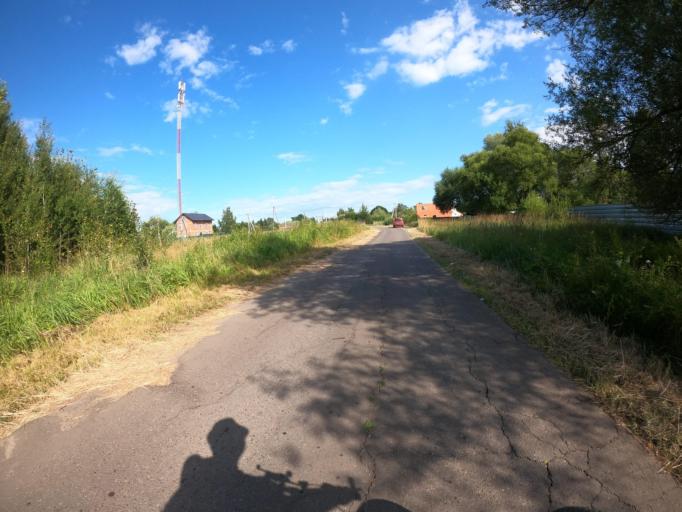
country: RU
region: Moskovskaya
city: Konobeyevo
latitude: 55.3938
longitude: 38.7127
